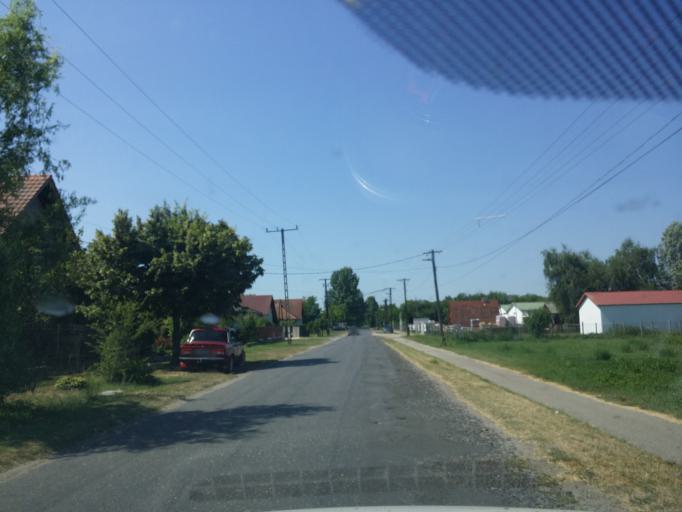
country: HU
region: Bacs-Kiskun
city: Jaszszentlaszlo
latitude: 46.5650
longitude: 19.7547
